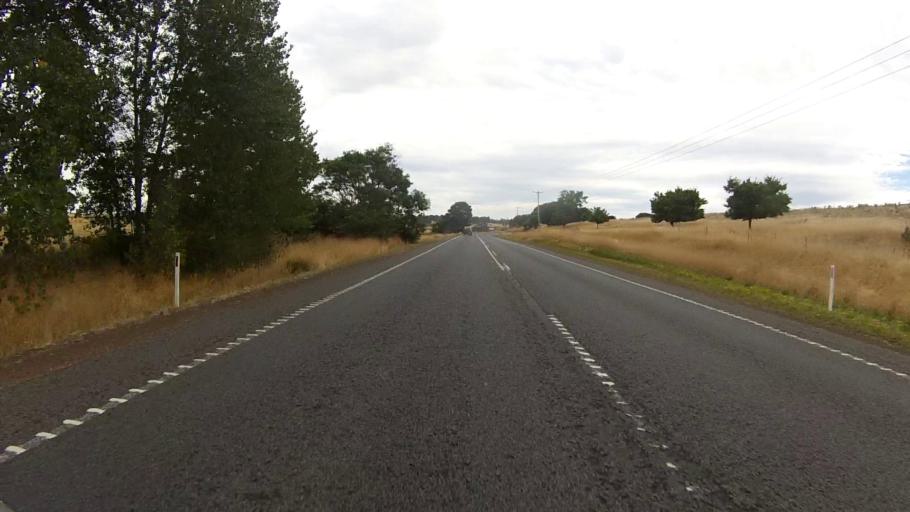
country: AU
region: Tasmania
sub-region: Northern Midlands
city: Evandale
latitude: -41.8469
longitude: 147.4494
